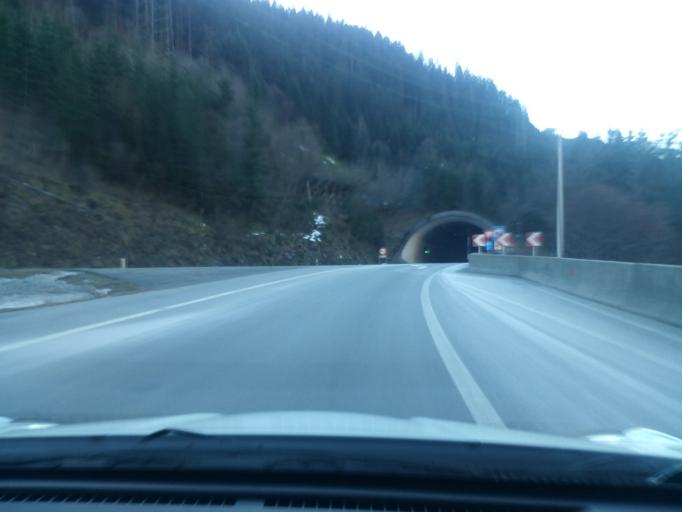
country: AT
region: Vorarlberg
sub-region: Politischer Bezirk Bludenz
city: Klosterle
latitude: 47.1304
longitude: 10.1109
